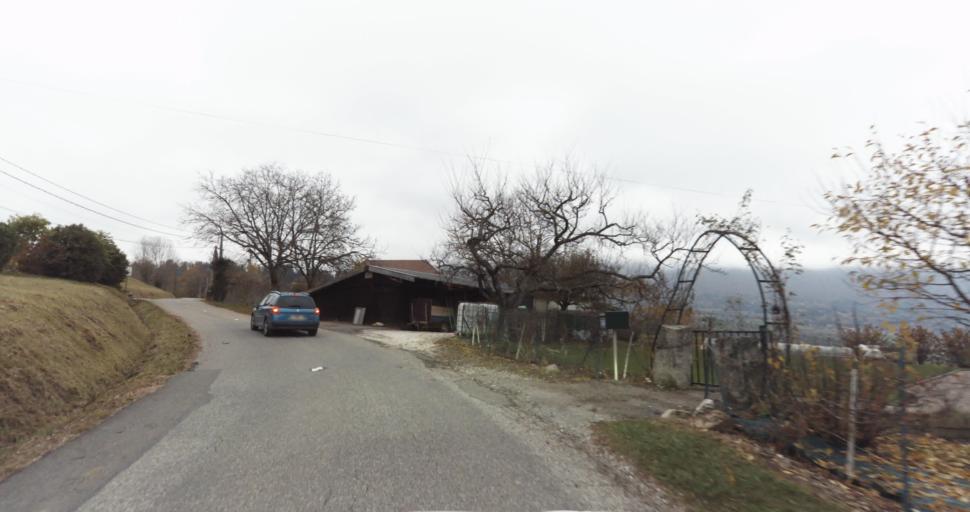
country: FR
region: Rhone-Alpes
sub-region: Departement de la Haute-Savoie
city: Saint-Jorioz
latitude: 45.8186
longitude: 6.1723
